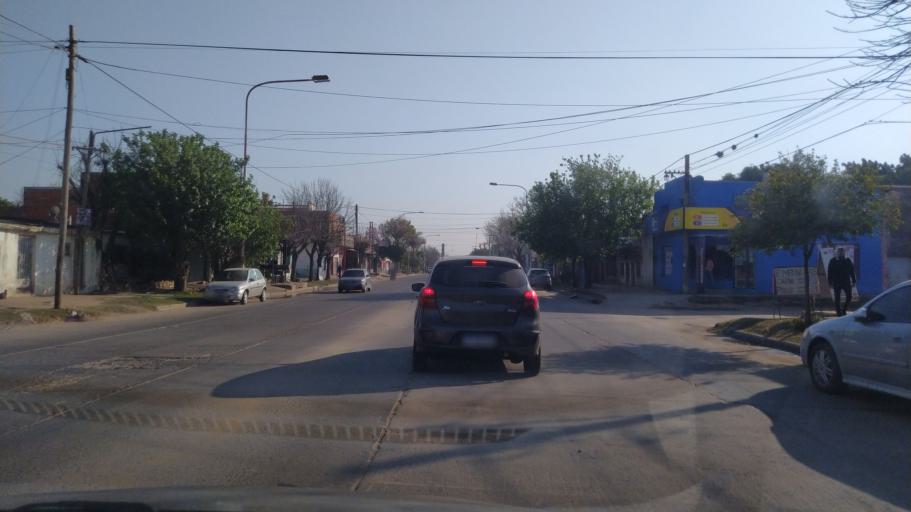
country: AR
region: Corrientes
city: Corrientes
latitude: -27.4822
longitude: -58.8154
